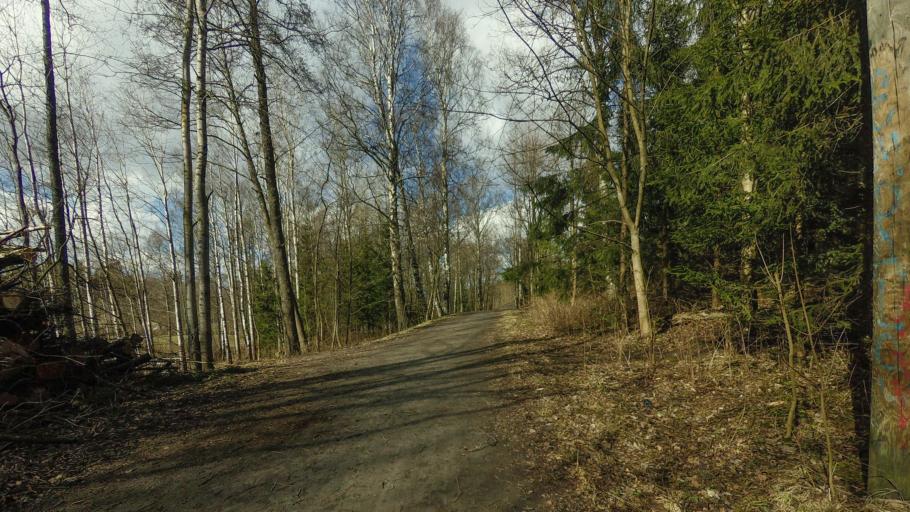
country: FI
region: Uusimaa
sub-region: Helsinki
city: Helsinki
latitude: 60.1935
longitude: 25.0235
